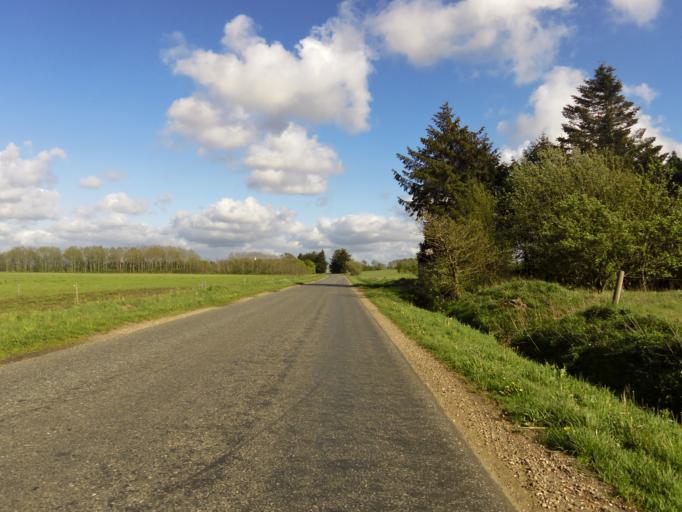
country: DK
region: South Denmark
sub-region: Esbjerg Kommune
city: Ribe
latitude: 55.2627
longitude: 8.7592
